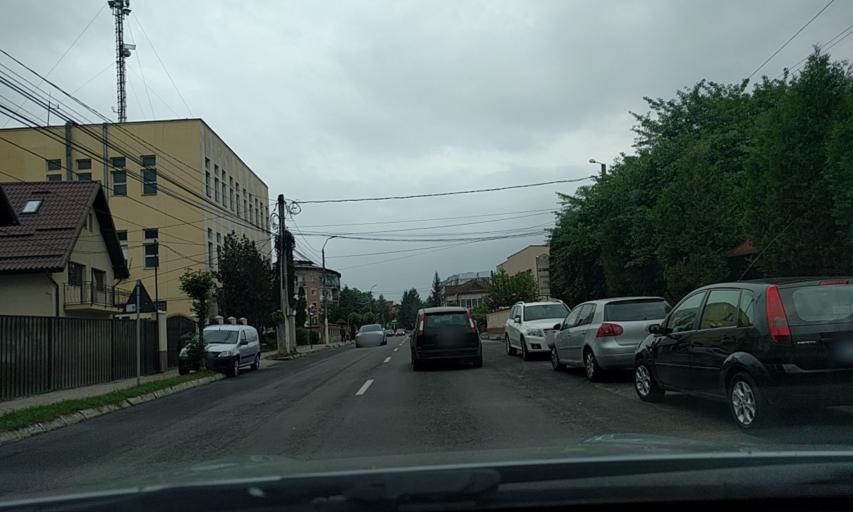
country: RO
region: Dambovita
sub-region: Oras Pucioasa
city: Pucioasa
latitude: 45.0727
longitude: 25.4353
